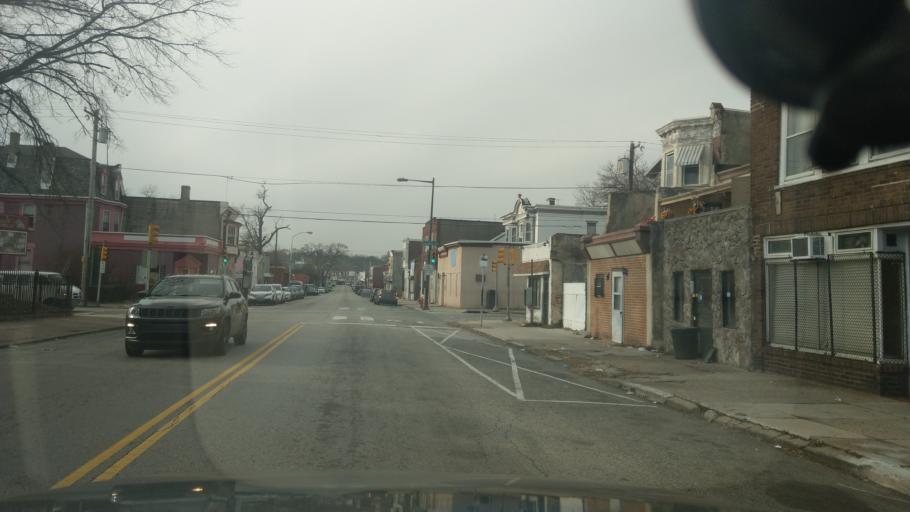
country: US
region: Pennsylvania
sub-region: Montgomery County
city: Wyncote
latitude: 40.0517
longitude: -75.1525
